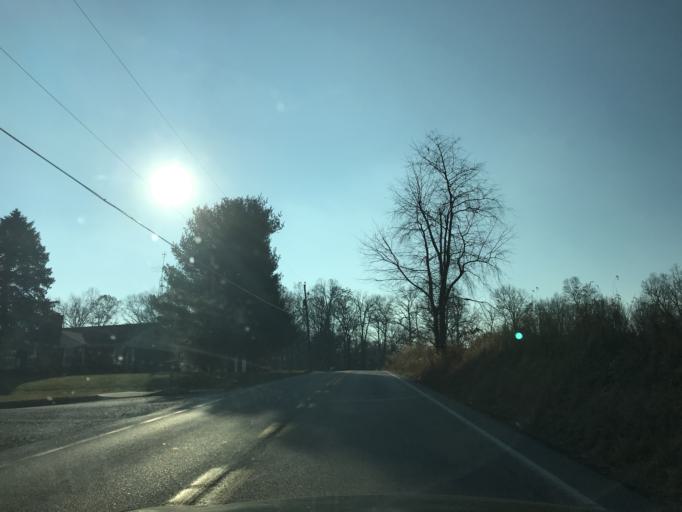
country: US
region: Pennsylvania
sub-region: York County
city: New Freedom
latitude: 39.7369
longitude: -76.7097
